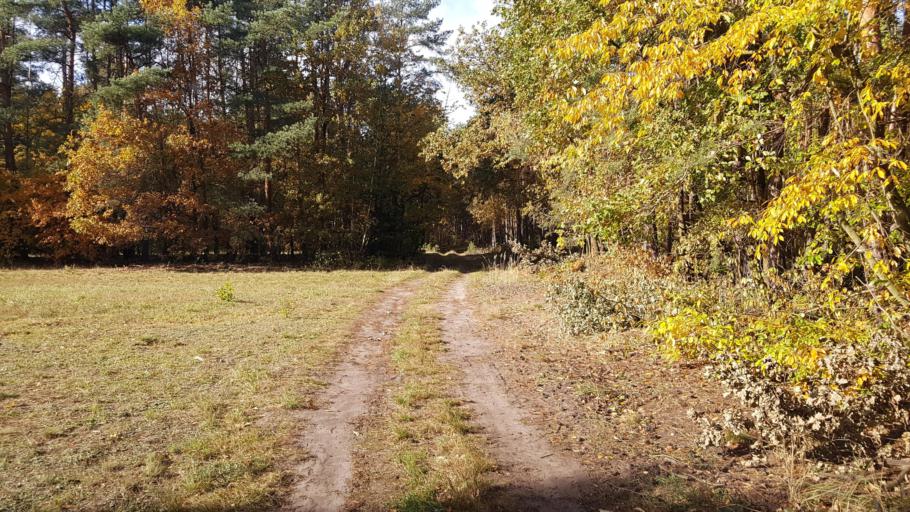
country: DE
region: Brandenburg
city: Tettau
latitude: 51.4342
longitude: 13.7503
